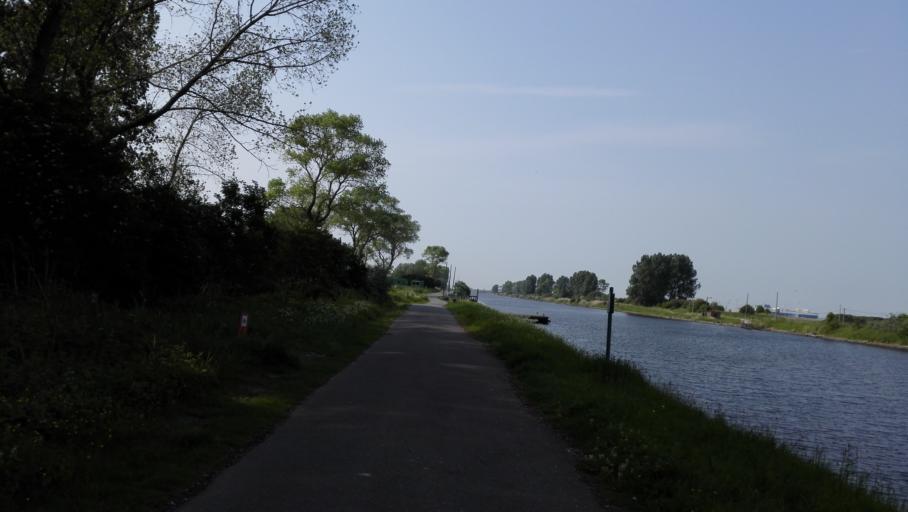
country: BE
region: Flanders
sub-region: Provincie West-Vlaanderen
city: Zeebrugge
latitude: 51.2926
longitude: 3.2066
